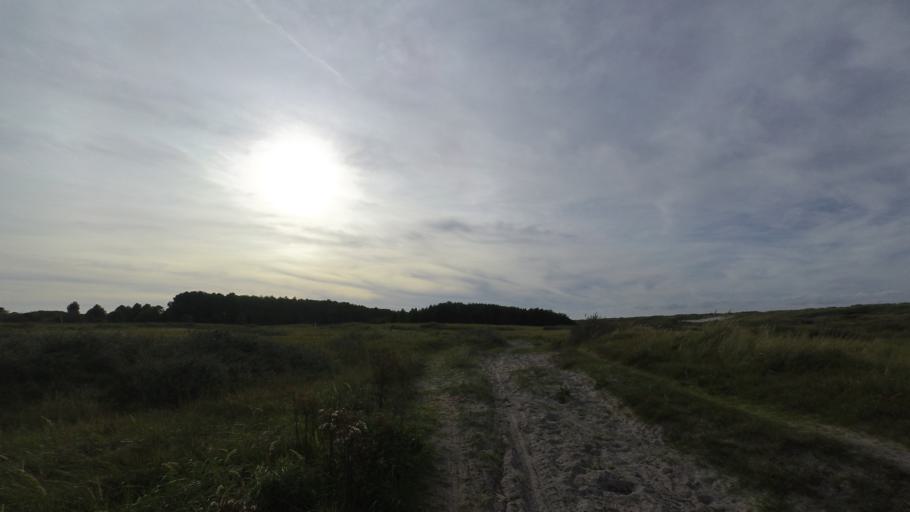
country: NL
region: Friesland
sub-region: Gemeente Ameland
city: Nes
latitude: 53.4595
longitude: 5.8244
